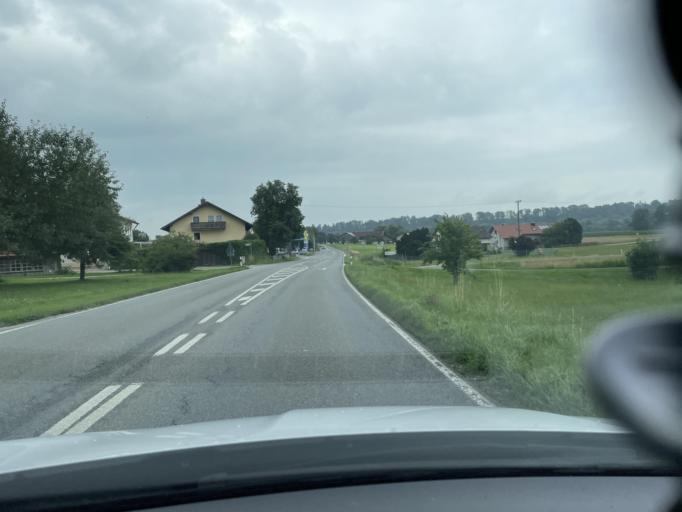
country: DE
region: Bavaria
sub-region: Upper Bavaria
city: Ramerberg
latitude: 47.9779
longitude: 12.1367
